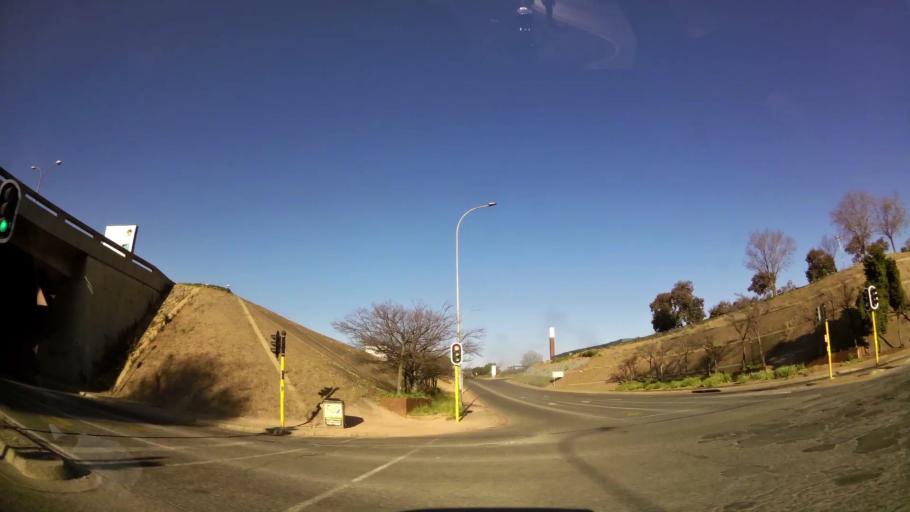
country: ZA
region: Gauteng
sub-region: City of Johannesburg Metropolitan Municipality
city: Roodepoort
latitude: -26.1373
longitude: 27.8619
